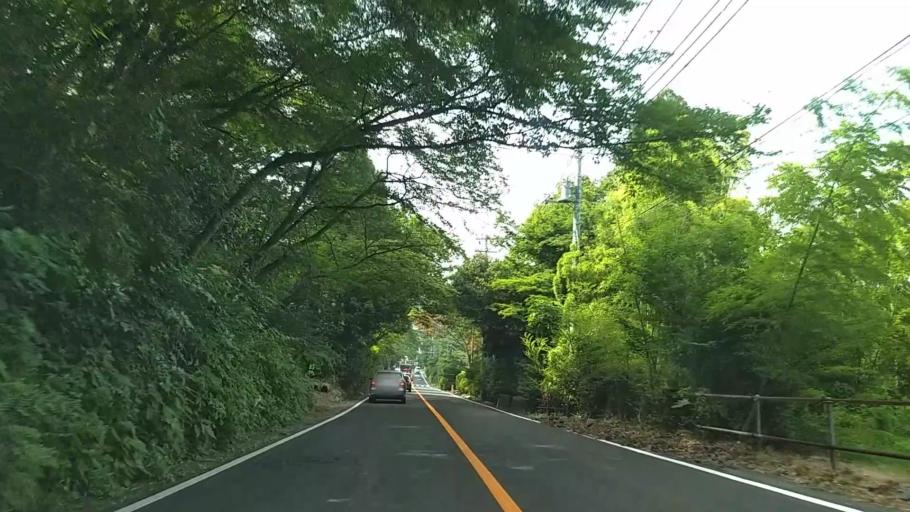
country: JP
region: Kanagawa
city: Hakone
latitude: 35.2359
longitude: 139.0478
